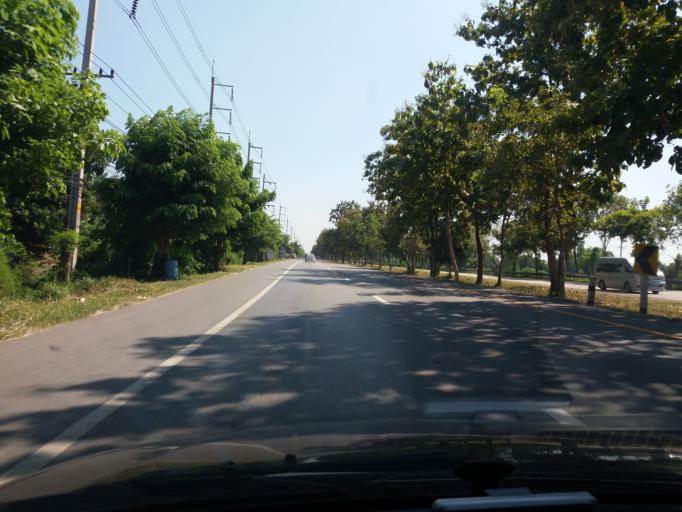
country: TH
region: Chai Nat
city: Sankhaburi
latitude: 15.0817
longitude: 100.1412
